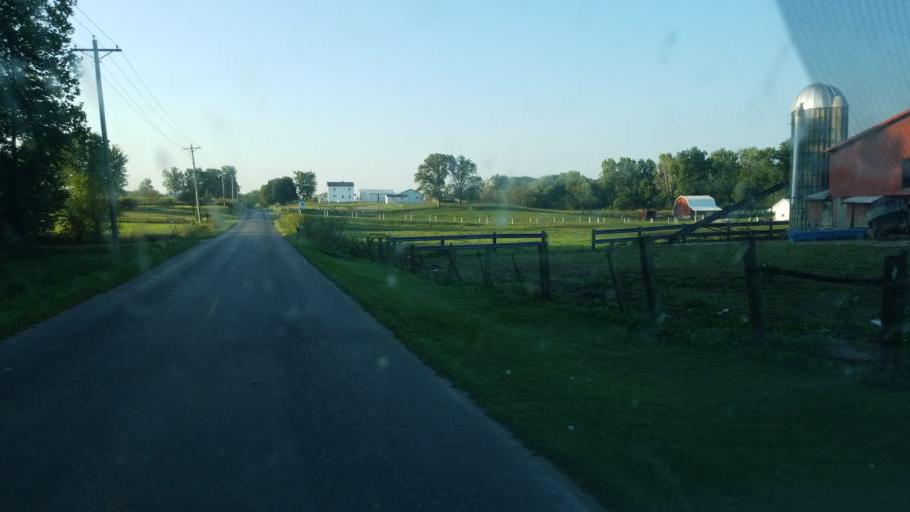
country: US
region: Indiana
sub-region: LaGrange County
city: Lagrange
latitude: 41.5819
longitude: -85.4240
